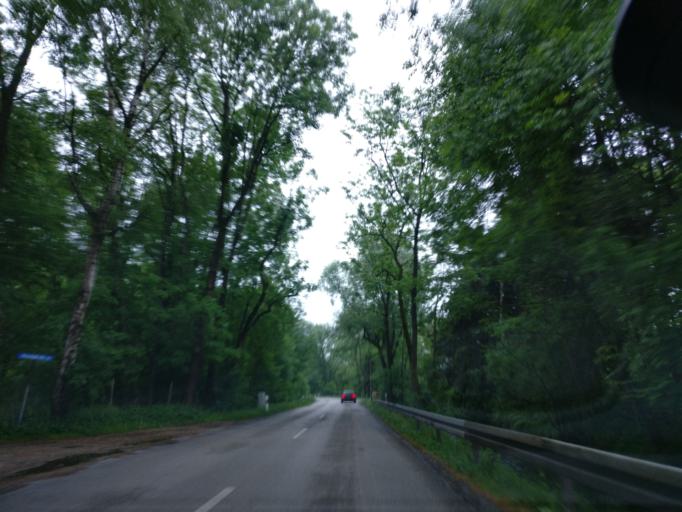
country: DE
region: Bavaria
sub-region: Upper Bavaria
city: Grobenzell
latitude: 48.2055
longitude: 11.4037
